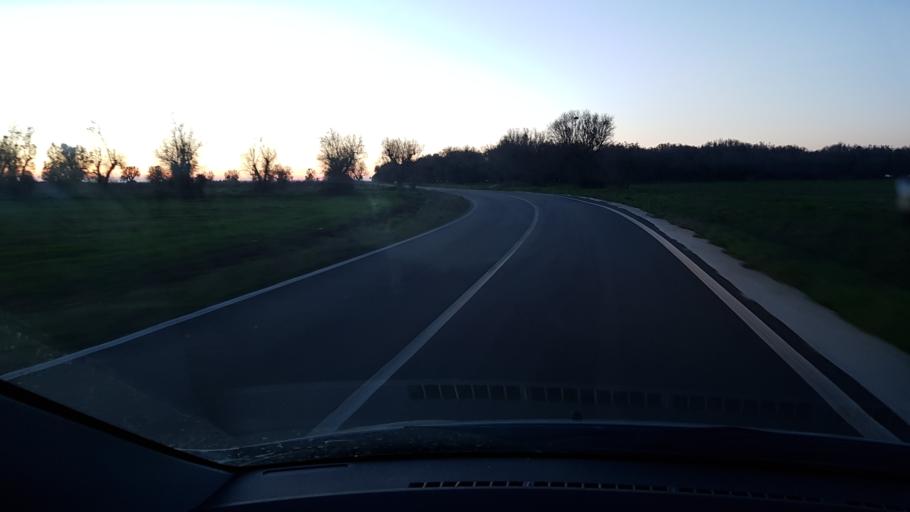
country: IT
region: Apulia
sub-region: Provincia di Brindisi
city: Tuturano
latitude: 40.5270
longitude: 17.9109
